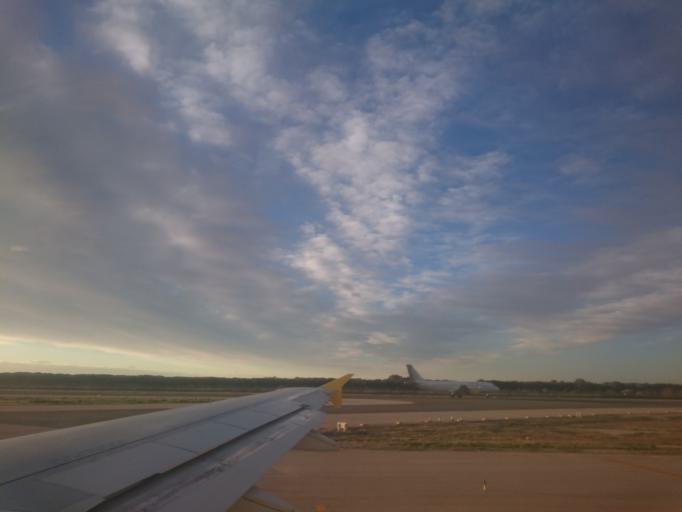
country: ES
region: Catalonia
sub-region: Provincia de Barcelona
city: El Prat de Llobregat
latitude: 41.2902
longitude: 2.0920
